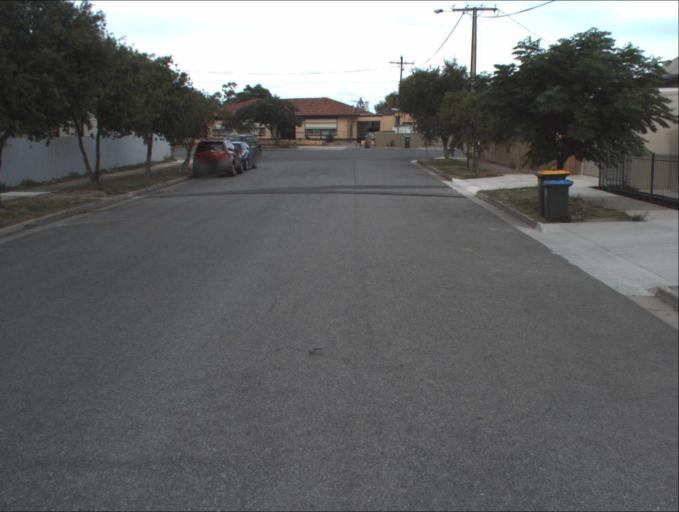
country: AU
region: South Australia
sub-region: Port Adelaide Enfield
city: Birkenhead
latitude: -34.8388
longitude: 138.4944
